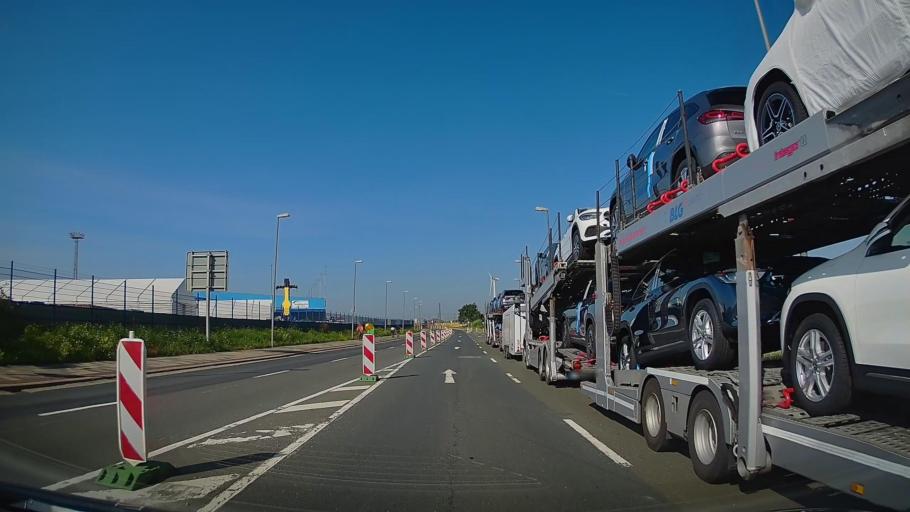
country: DE
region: Bremen
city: Bremerhaven
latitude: 53.5824
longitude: 8.5463
